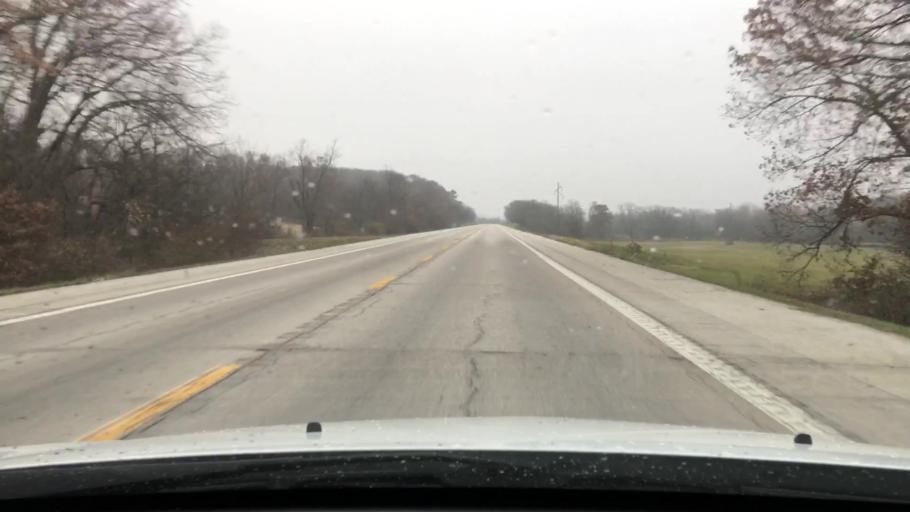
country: US
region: Missouri
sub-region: Pike County
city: Bowling Green
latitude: 39.3741
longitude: -91.1622
